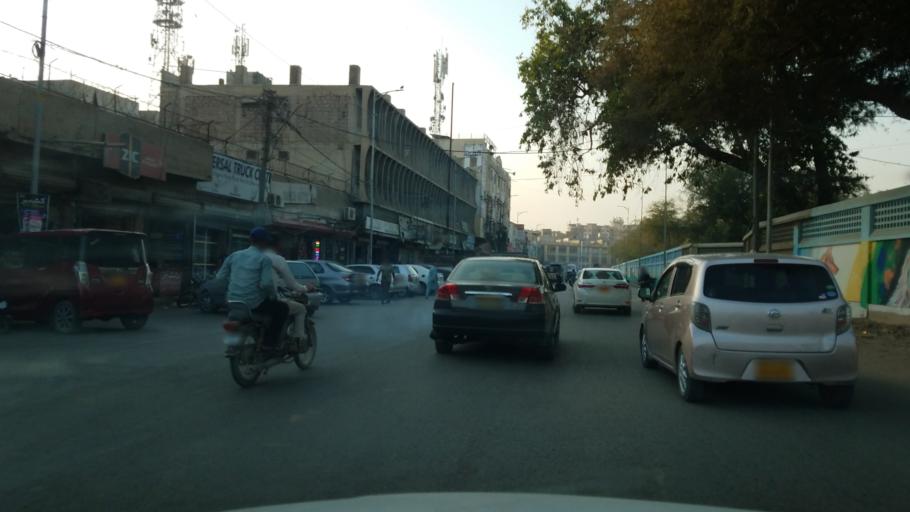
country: PK
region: Sindh
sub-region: Karachi District
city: Karachi
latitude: 24.8739
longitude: 67.0224
